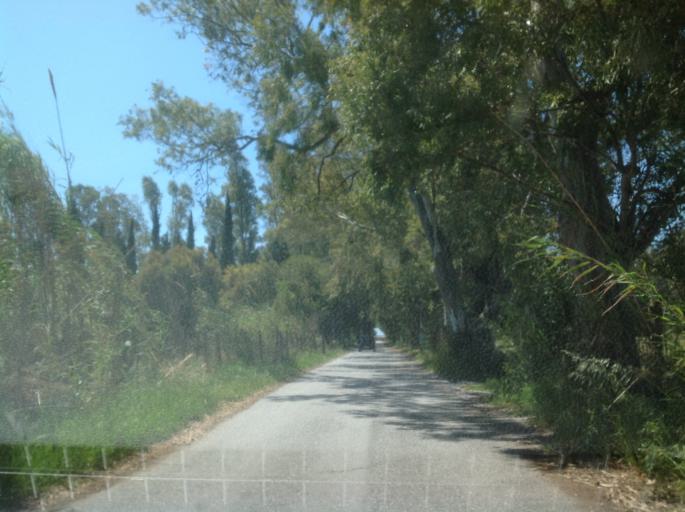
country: IT
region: Calabria
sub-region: Provincia di Catanzaro
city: Gizzeria
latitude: 38.9399
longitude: 16.1911
